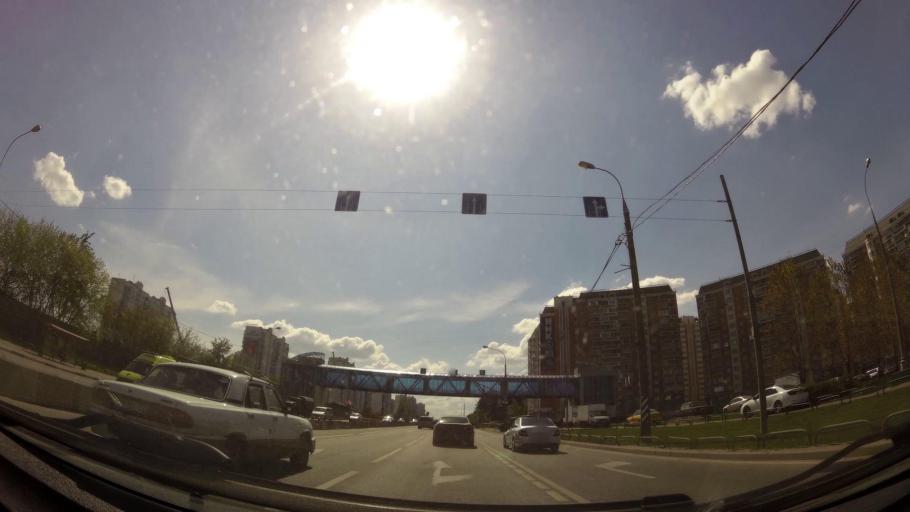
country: RU
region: Moscow
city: Solntsevo
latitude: 55.6498
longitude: 37.3718
